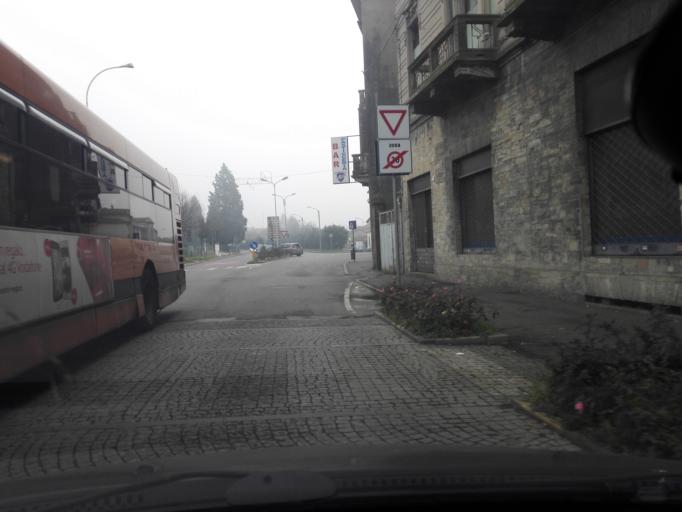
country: IT
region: Piedmont
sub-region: Provincia di Alessandria
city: Alessandria
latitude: 44.9038
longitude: 8.6060
